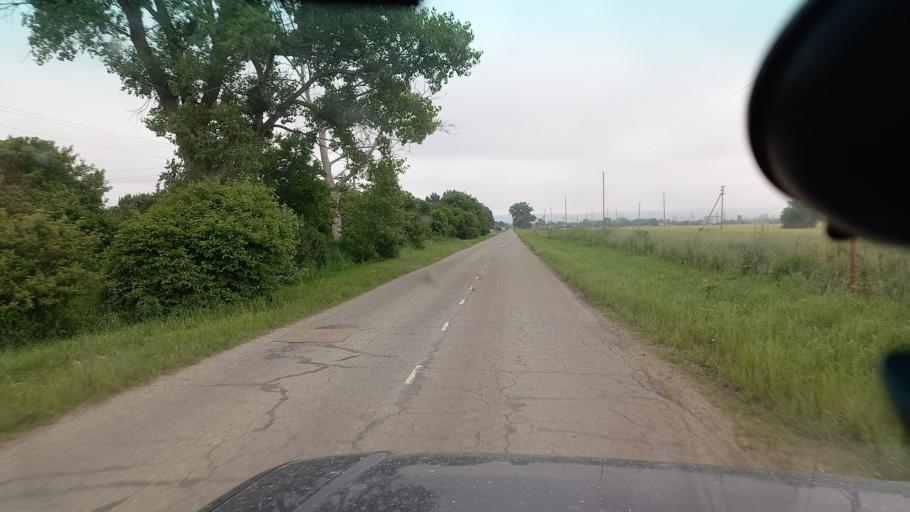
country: RU
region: Krasnodarskiy
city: Mostovskoy
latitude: 44.4231
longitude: 40.7541
